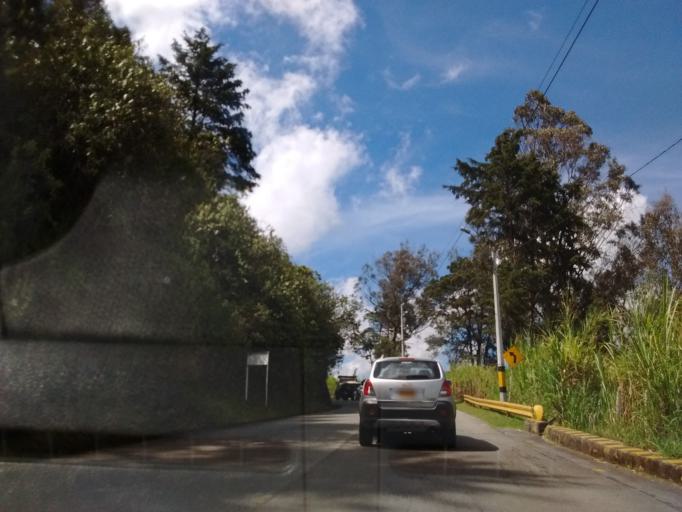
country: CO
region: Antioquia
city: Medellin
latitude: 6.2364
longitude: -75.5110
